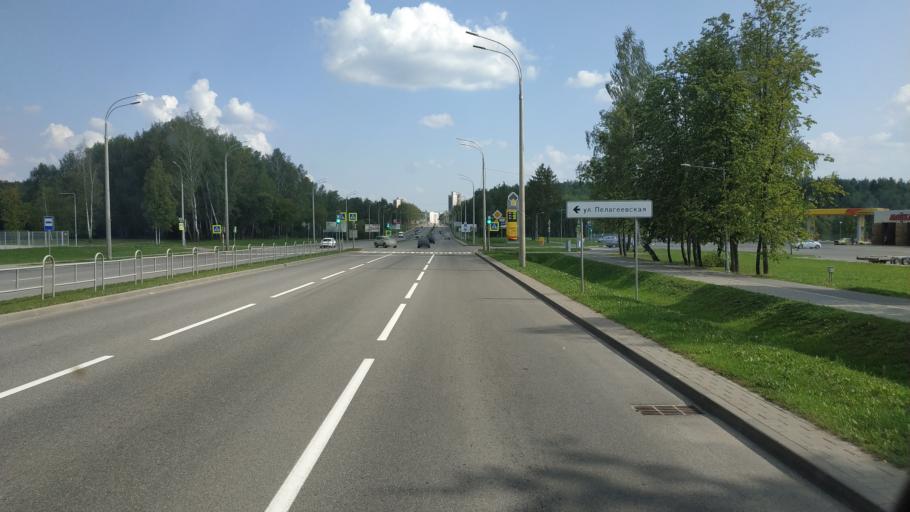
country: BY
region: Mogilev
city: Buynichy
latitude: 53.9275
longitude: 30.2696
